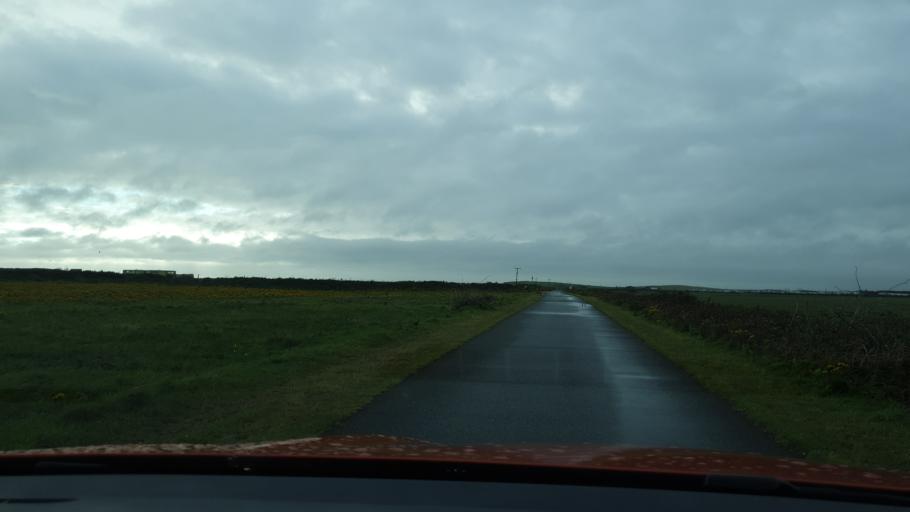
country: GB
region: England
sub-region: Cumbria
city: Barrow in Furness
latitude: 54.0496
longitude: -3.2006
